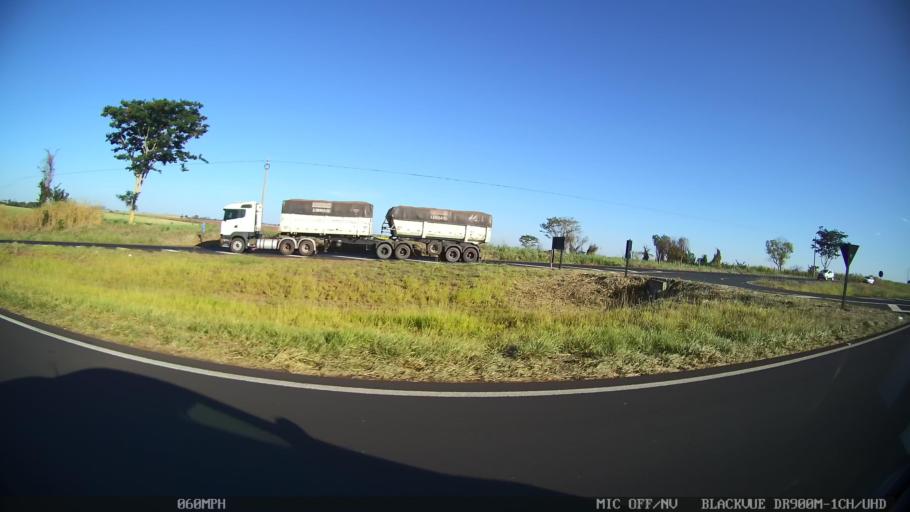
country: BR
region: Sao Paulo
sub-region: Olimpia
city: Olimpia
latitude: -20.7231
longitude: -49.0261
